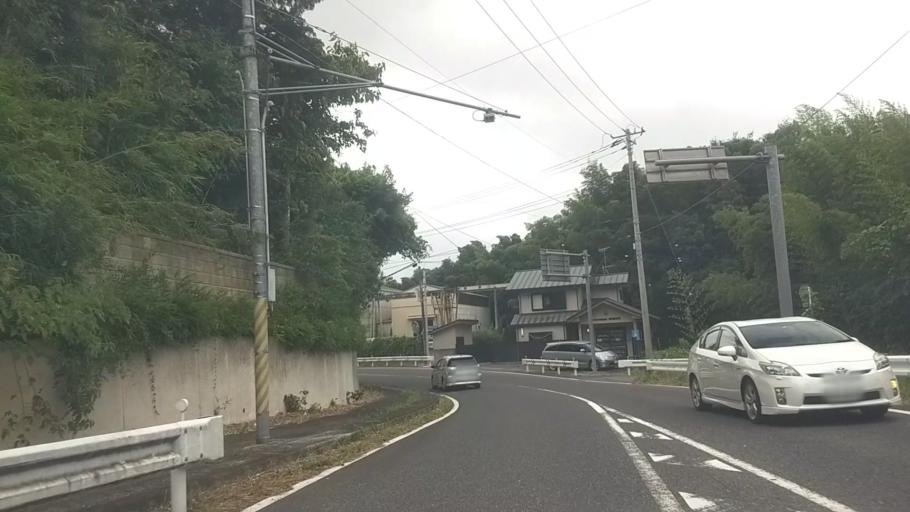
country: JP
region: Chiba
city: Kimitsu
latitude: 35.2485
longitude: 140.0017
